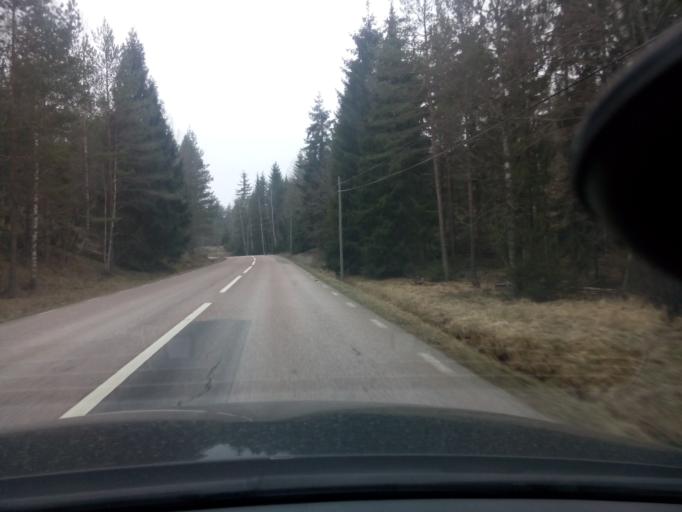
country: SE
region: Soedermanland
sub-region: Nykopings Kommun
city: Nykoping
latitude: 58.9352
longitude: 17.1148
